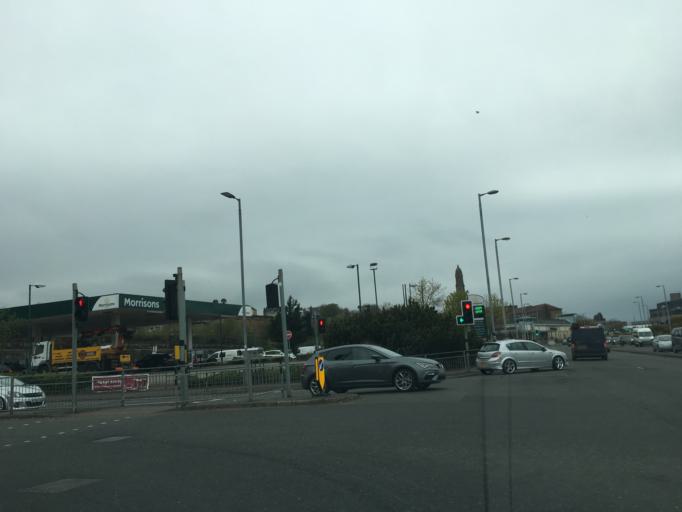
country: GB
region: Scotland
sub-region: Inverclyde
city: Greenock
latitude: 55.9446
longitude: -4.7479
